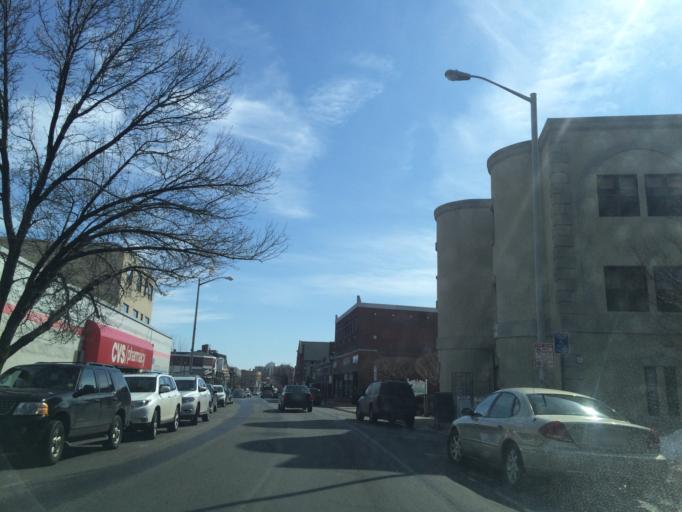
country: US
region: Massachusetts
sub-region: Middlesex County
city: Medford
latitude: 42.4189
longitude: -71.1127
